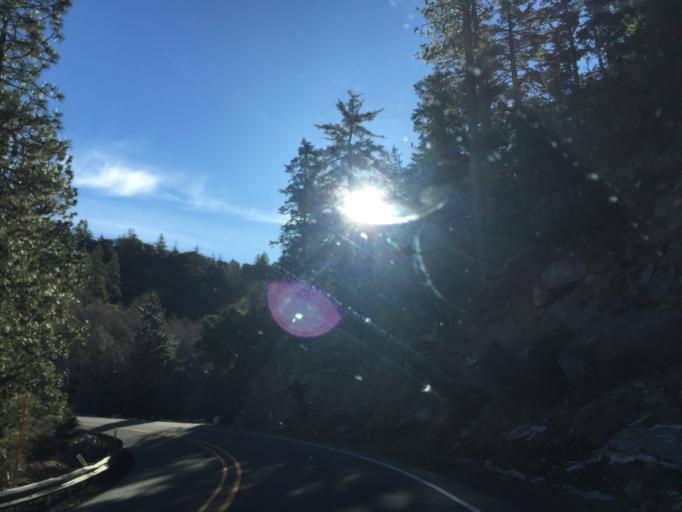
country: US
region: California
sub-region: San Bernardino County
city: Big Bear Lake
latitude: 34.1569
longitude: -116.9323
